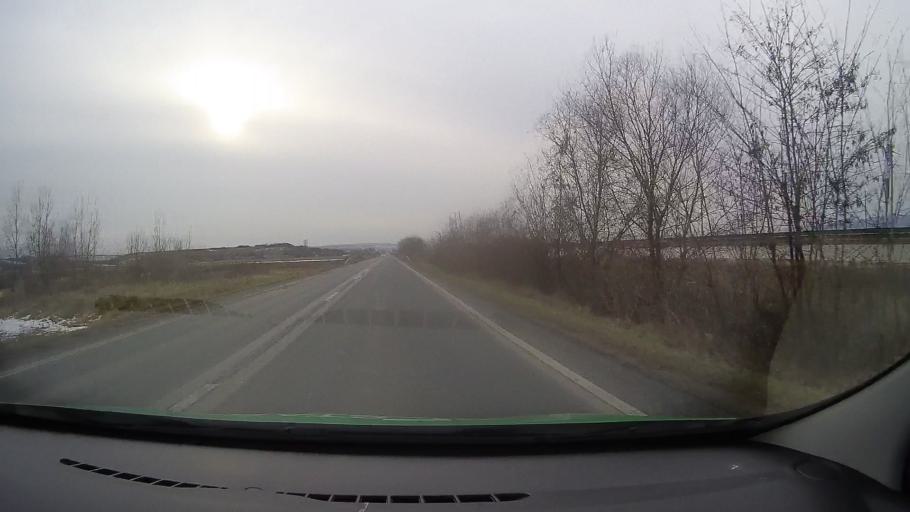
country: RO
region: Hunedoara
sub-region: Municipiul Orastie
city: Orastie
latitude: 45.8734
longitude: 23.2338
